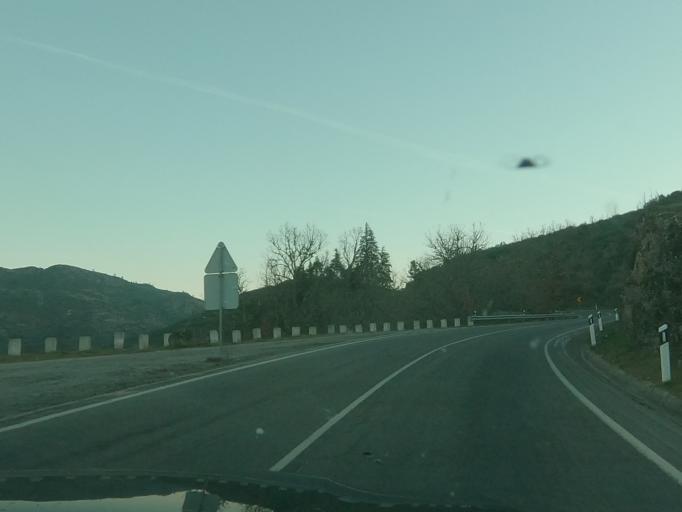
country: PT
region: Vila Real
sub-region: Vila Pouca de Aguiar
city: Vila Pouca de Aguiar
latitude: 41.4163
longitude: -7.6871
